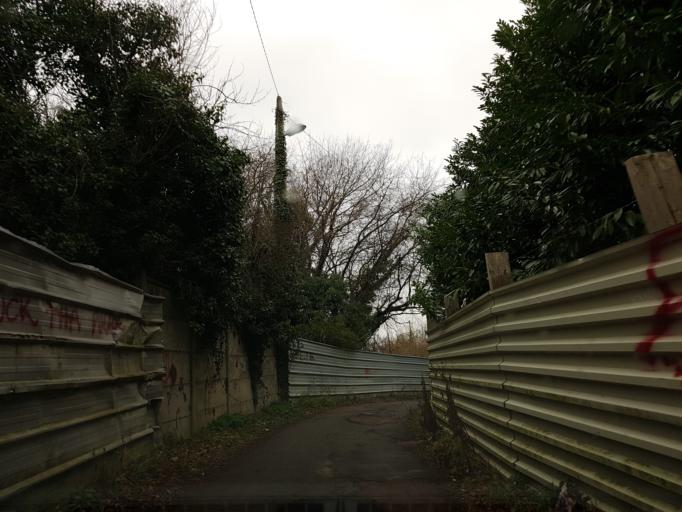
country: FR
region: Ile-de-France
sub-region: Departement du Val-de-Marne
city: Thiais
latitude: 48.7777
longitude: 2.3898
